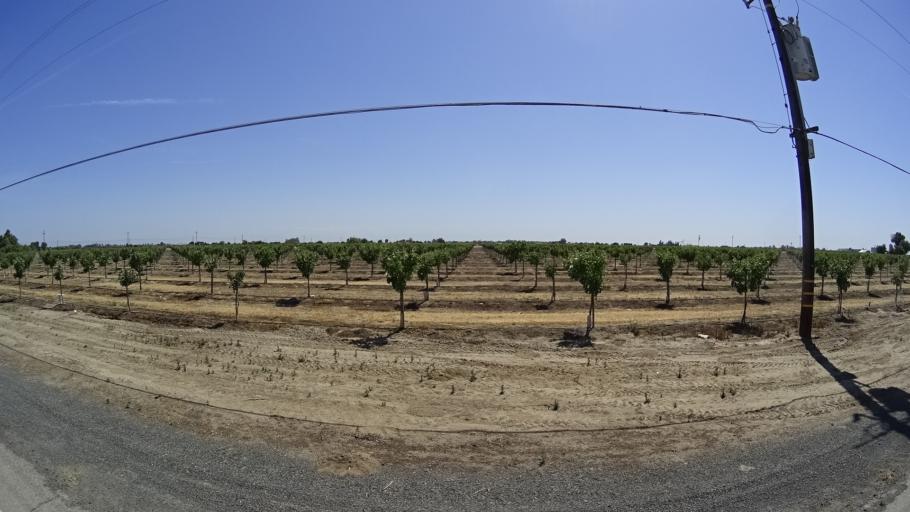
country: US
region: California
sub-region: Kings County
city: Lemoore
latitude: 36.2528
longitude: -119.7808
